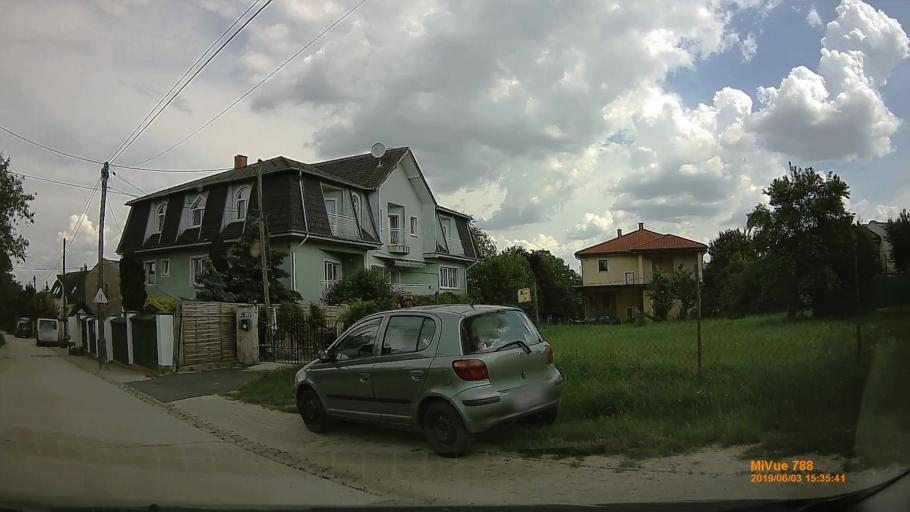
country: HU
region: Budapest
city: Budapest XXII. keruelet
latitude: 47.4319
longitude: 19.0207
